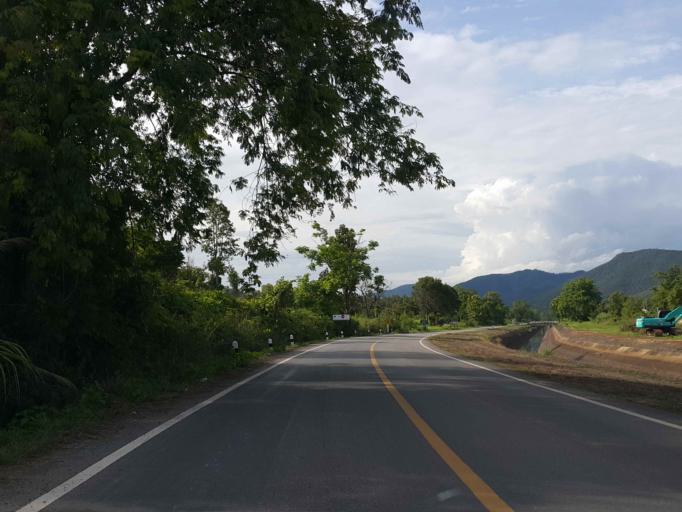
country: TH
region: Chiang Mai
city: San Sai
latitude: 18.8974
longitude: 99.1487
